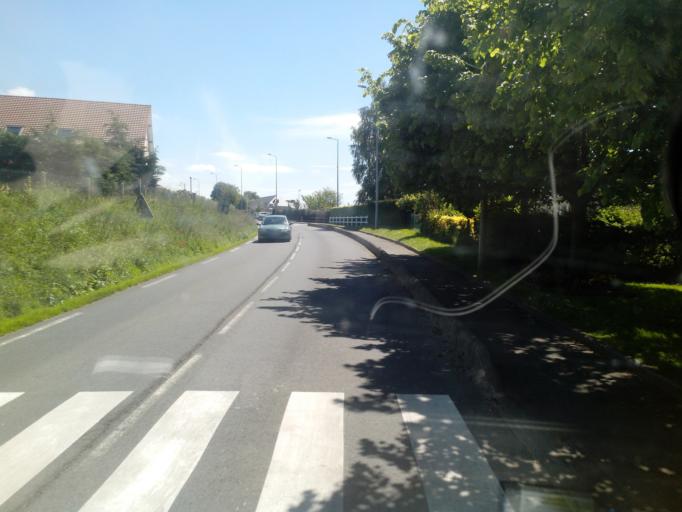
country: FR
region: Haute-Normandie
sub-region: Departement de la Seine-Maritime
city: Maneglise
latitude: 49.5871
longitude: 0.2834
